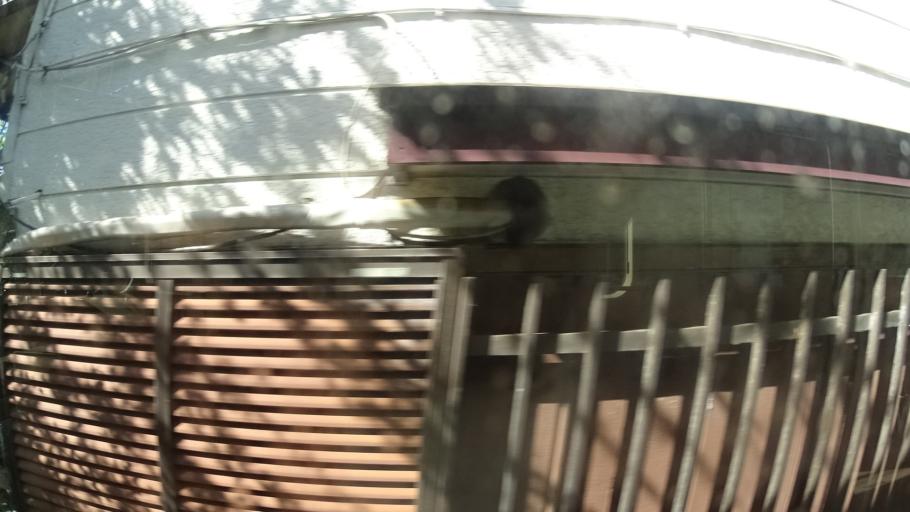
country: JP
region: Kanagawa
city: Fujisawa
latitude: 35.3079
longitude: 139.4941
